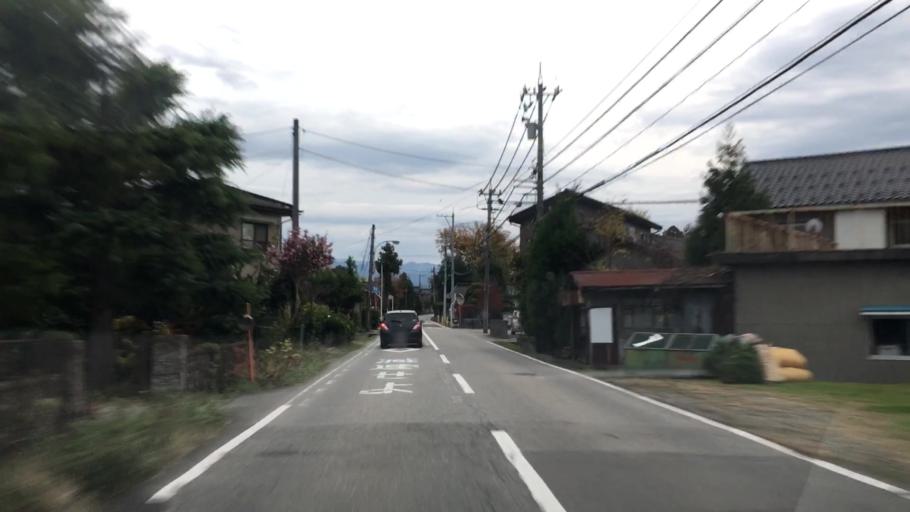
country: JP
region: Toyama
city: Kamiichi
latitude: 36.6945
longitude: 137.3151
